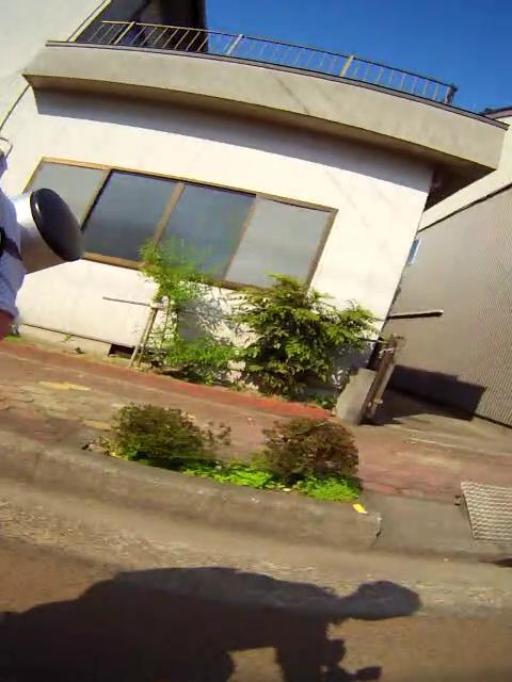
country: JP
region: Toyama
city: Fukumitsu
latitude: 36.5215
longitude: 136.9018
